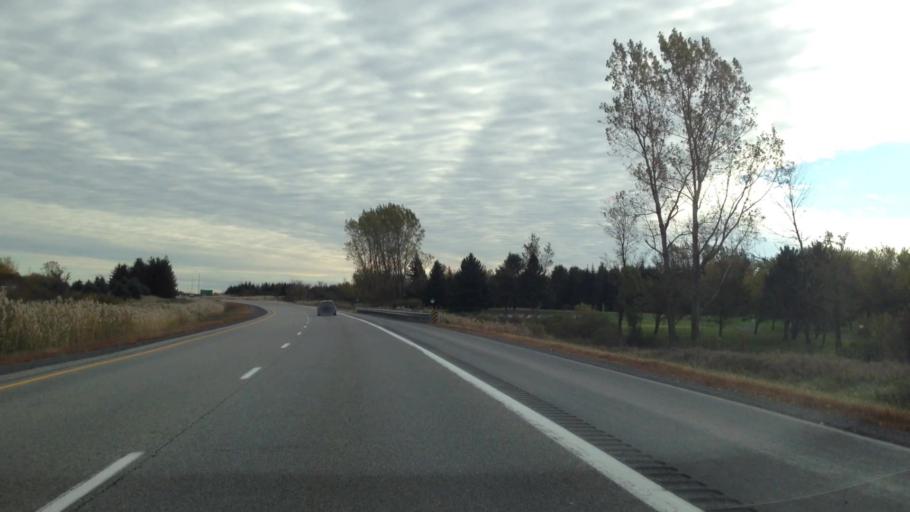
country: CA
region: Ontario
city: Casselman
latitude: 45.3021
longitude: -75.0938
